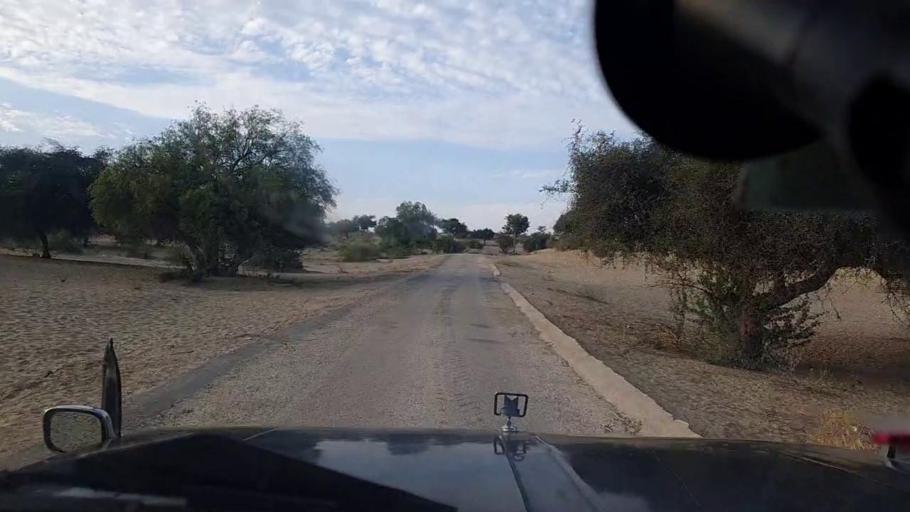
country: PK
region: Sindh
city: Diplo
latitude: 24.4676
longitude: 69.7906
